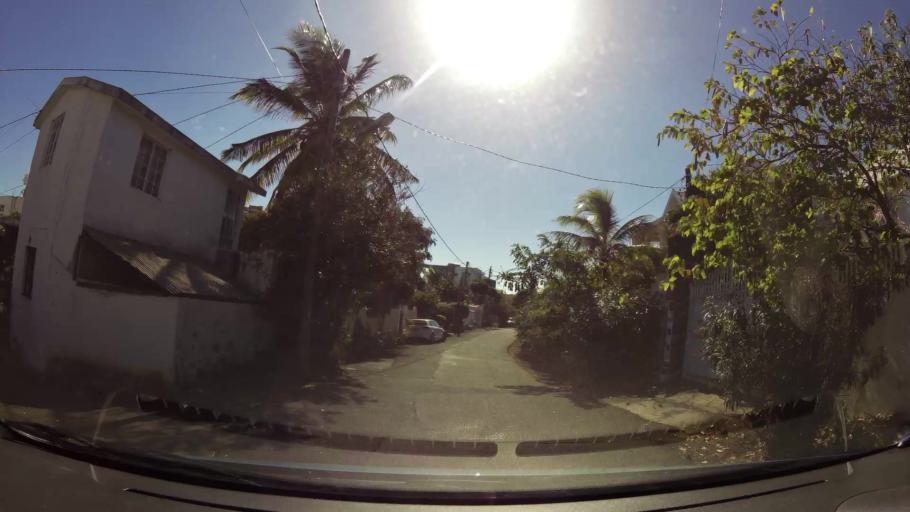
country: MU
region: Black River
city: Flic en Flac
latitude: -20.2645
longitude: 57.3765
